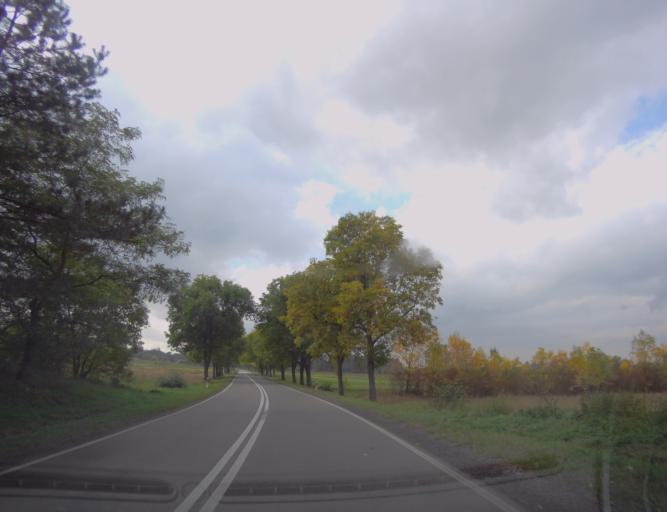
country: PL
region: Lublin Voivodeship
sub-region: Powiat krasnostawski
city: Gorzkow
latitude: 50.9324
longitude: 22.9681
